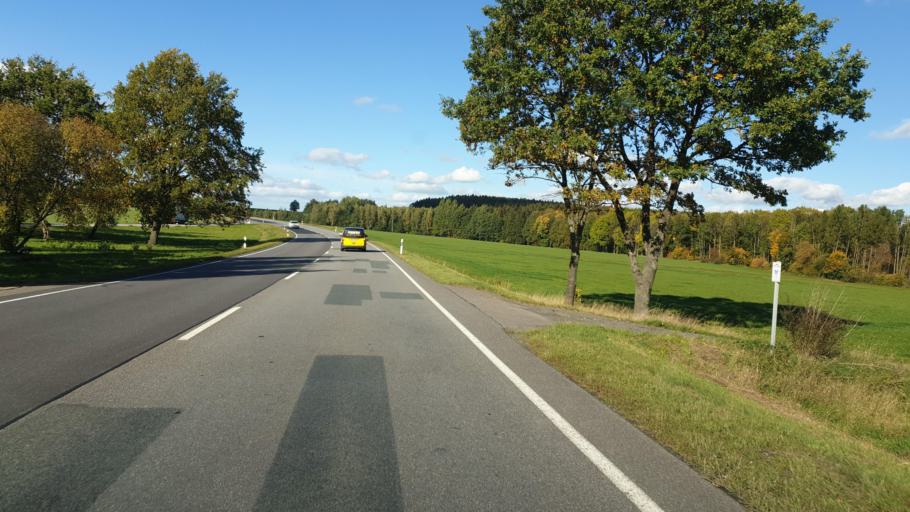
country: DE
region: Saxony
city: Grossolbersdorf
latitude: 50.6999
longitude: 13.1104
